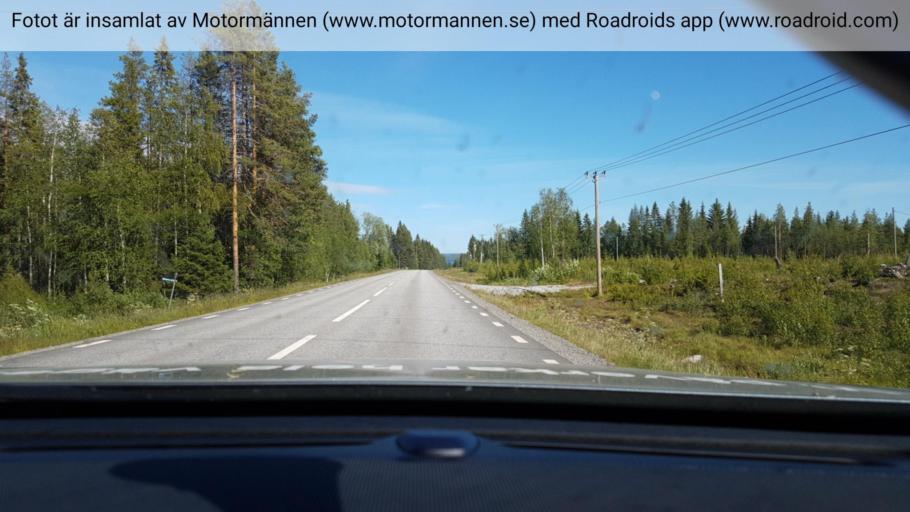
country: SE
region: Vaesterbotten
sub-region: Lycksele Kommun
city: Lycksele
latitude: 64.6483
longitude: 18.4771
